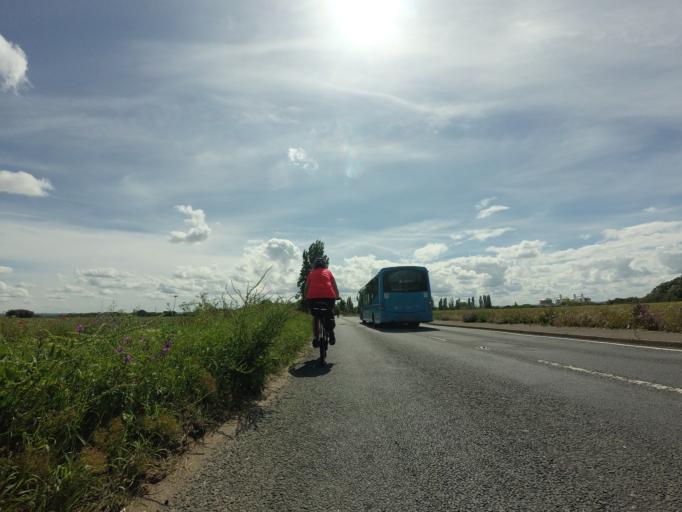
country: GB
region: England
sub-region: Kent
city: Queenborough
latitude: 51.4516
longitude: 0.7007
